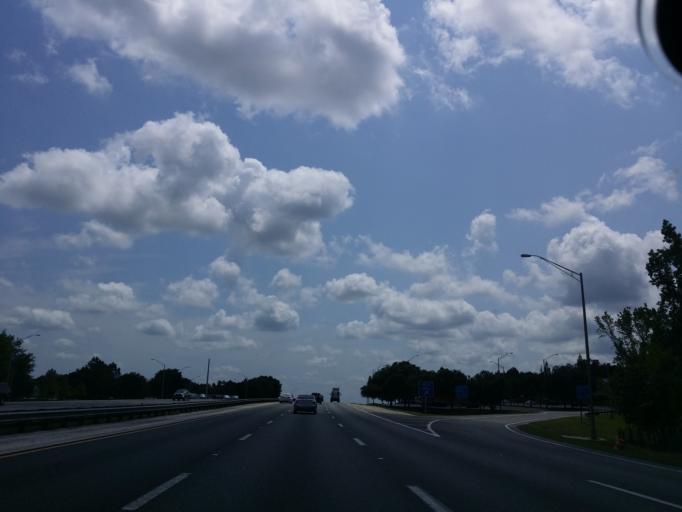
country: US
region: Florida
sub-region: Alachua County
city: Gainesville
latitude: 29.5920
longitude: -82.3644
